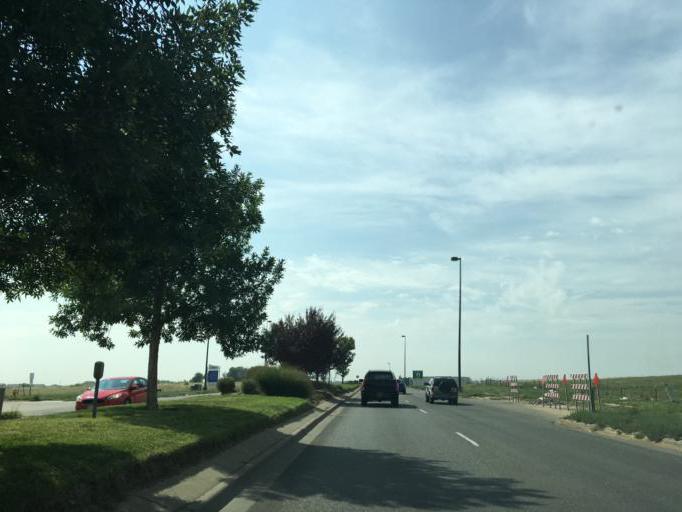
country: US
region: Colorado
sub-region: Adams County
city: Aurora
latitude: 39.8024
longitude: -104.7722
